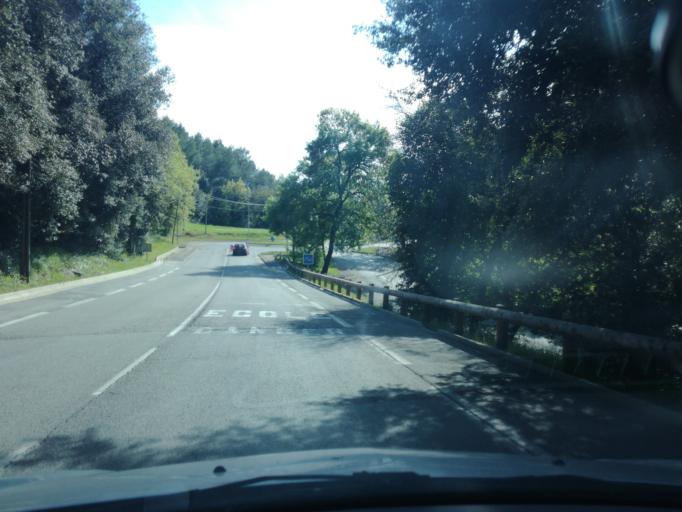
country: FR
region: Provence-Alpes-Cote d'Azur
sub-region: Departement des Alpes-Maritimes
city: La Roquette-sur-Siagne
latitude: 43.6162
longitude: 6.9522
